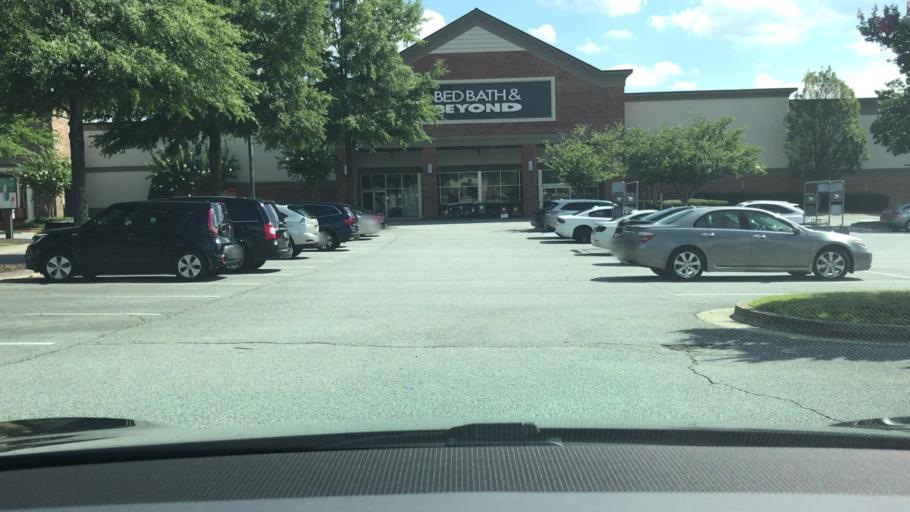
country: US
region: Georgia
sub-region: Gwinnett County
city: Sugar Hill
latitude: 34.0612
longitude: -83.9937
